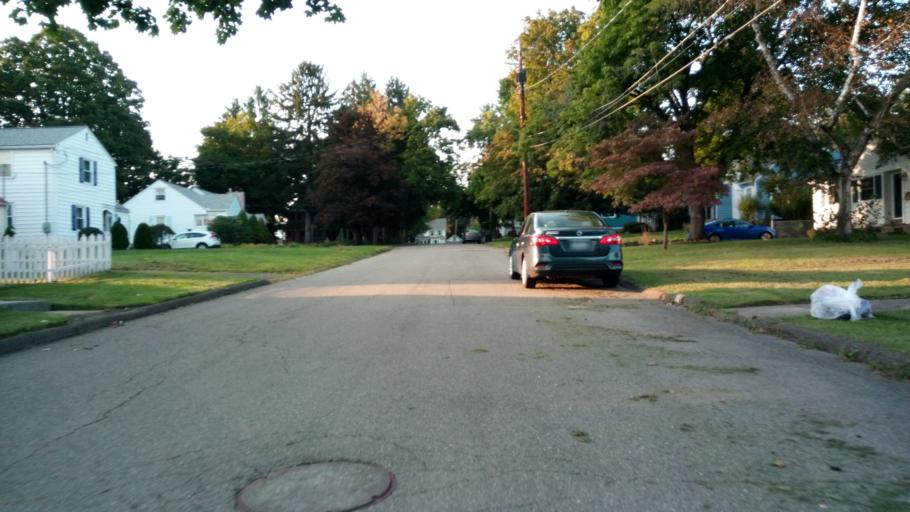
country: US
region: New York
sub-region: Chemung County
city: West Elmira
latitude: 42.0770
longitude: -76.8382
